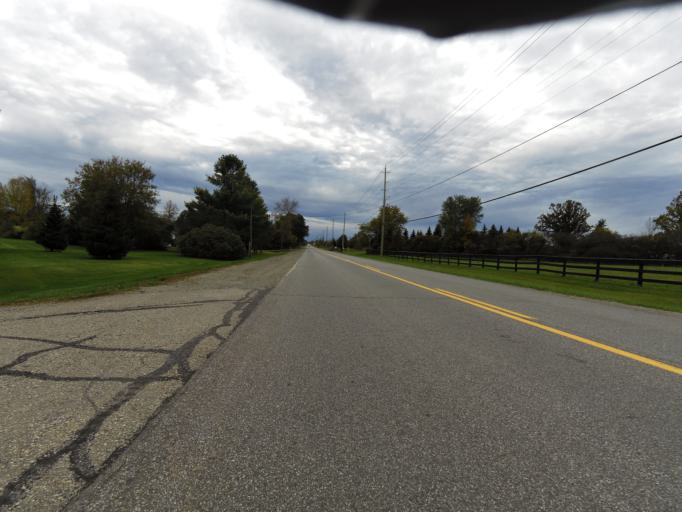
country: CA
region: Ontario
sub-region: Lanark County
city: Smiths Falls
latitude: 44.9351
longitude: -75.8311
